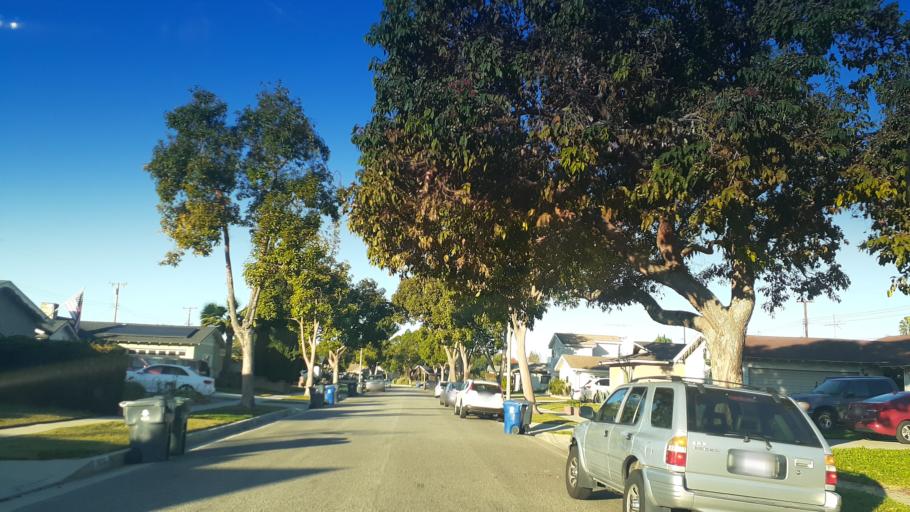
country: US
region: California
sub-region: Los Angeles County
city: Hawaiian Gardens
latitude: 33.8434
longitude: -118.0880
